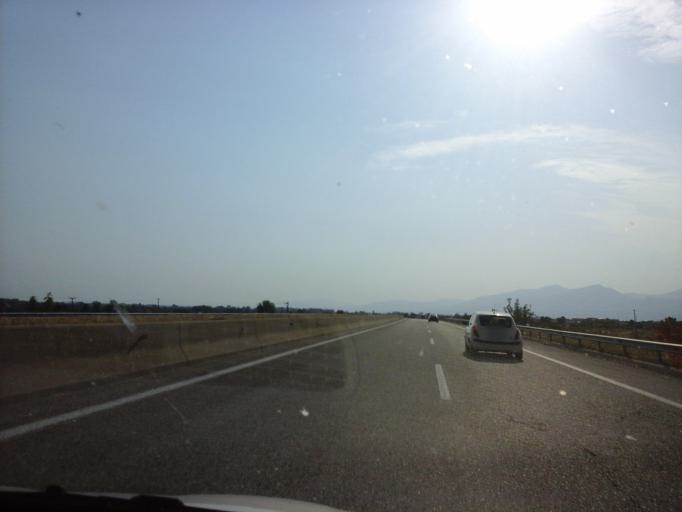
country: GR
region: East Macedonia and Thrace
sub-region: Nomos Xanthis
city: Selero
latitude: 41.1193
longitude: 25.0445
